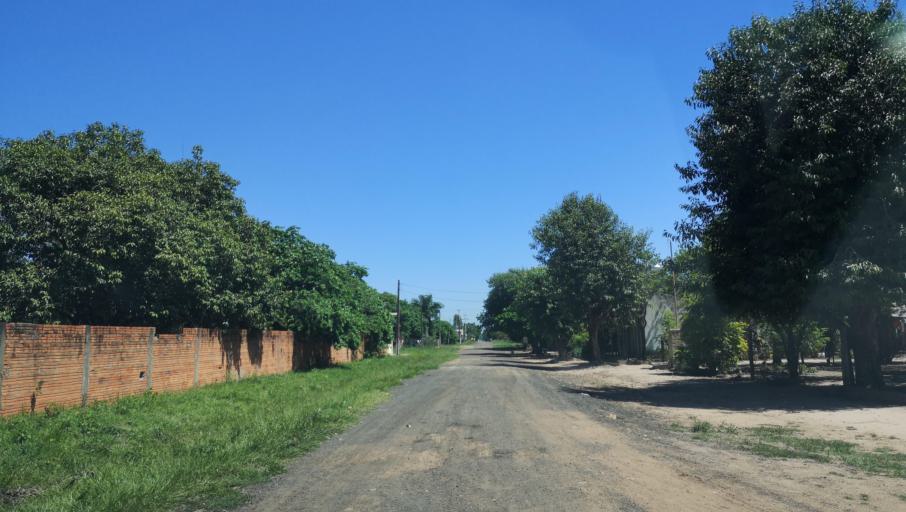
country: PY
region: Caaguazu
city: Carayao
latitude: -25.1994
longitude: -56.3947
